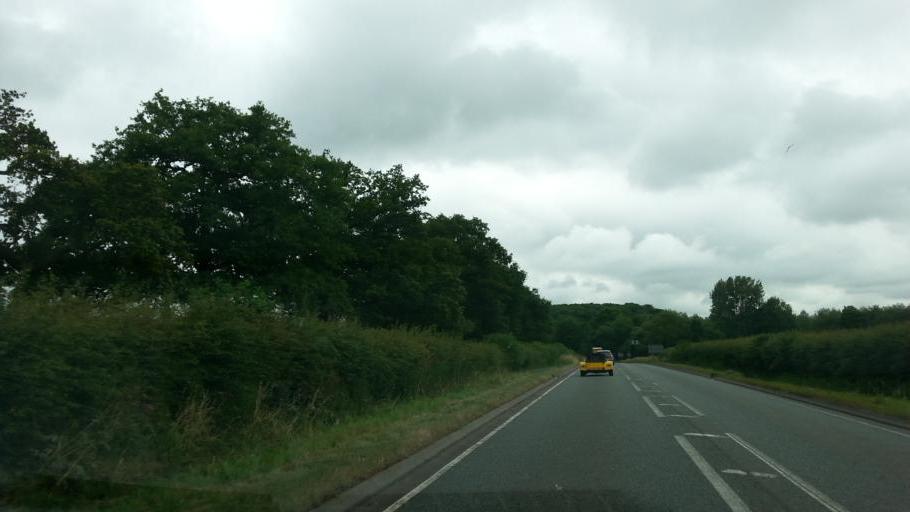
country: GB
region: England
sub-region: District of Rutland
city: Morcott
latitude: 52.5165
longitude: -0.5957
